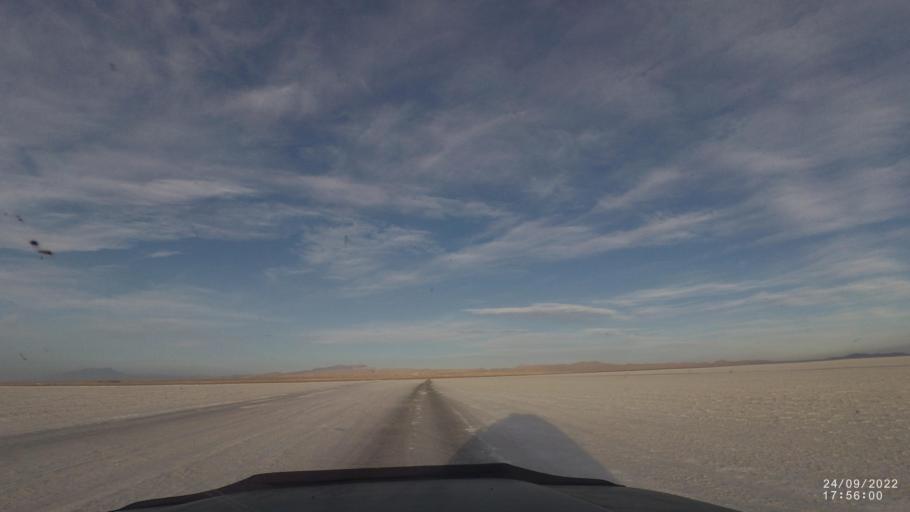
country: BO
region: Potosi
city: Colchani
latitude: -20.3255
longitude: -67.0209
